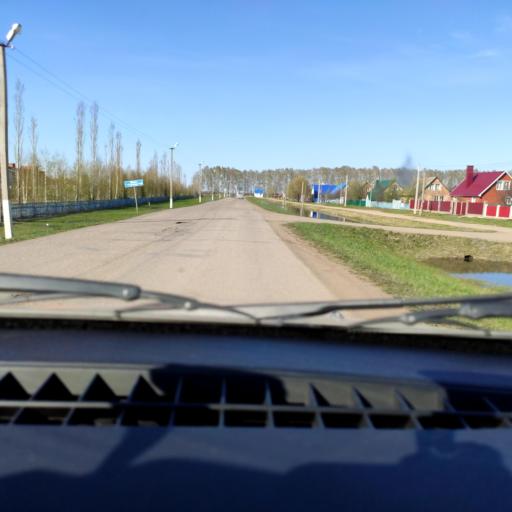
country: RU
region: Bashkortostan
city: Kabakovo
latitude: 54.6022
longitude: 56.1846
